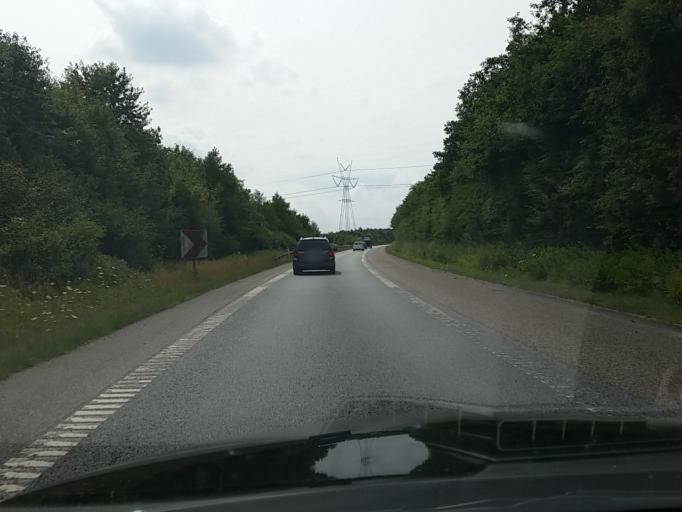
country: DK
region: South Denmark
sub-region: Kolding Kommune
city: Kolding
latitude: 55.5171
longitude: 9.4370
